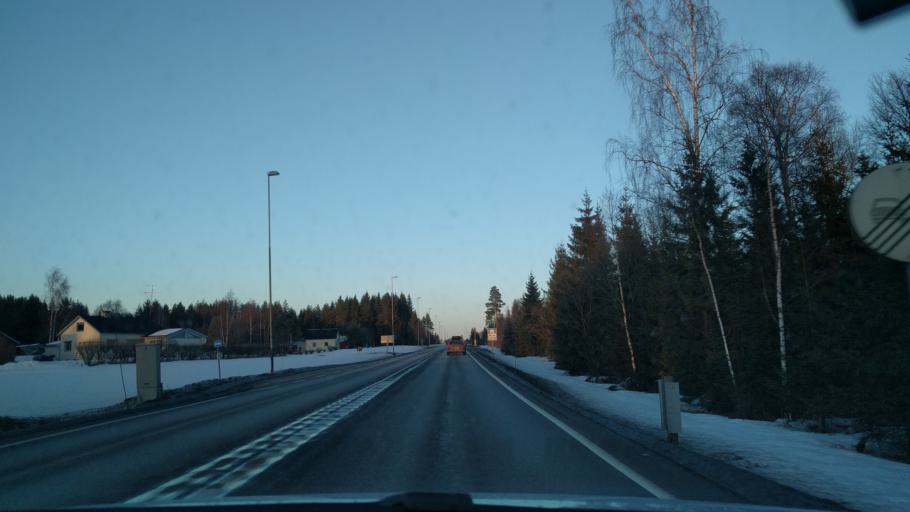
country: NO
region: Hedmark
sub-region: Loten
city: Loten
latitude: 60.8508
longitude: 11.3743
